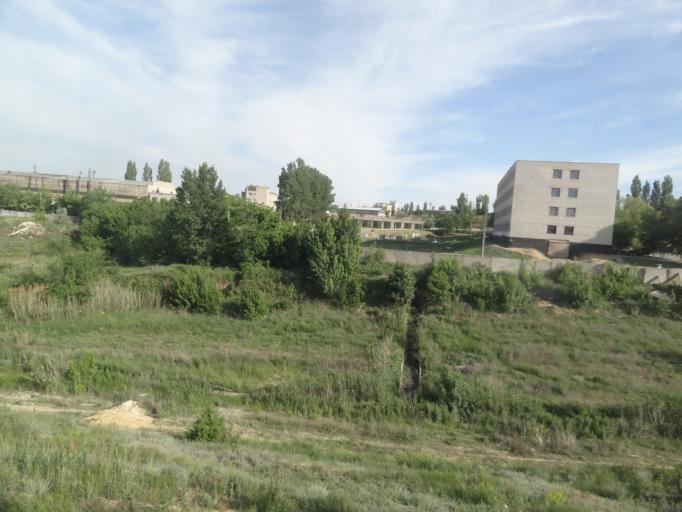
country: RU
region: Volgograd
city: Gorodishche
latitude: 48.7708
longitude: 44.4527
